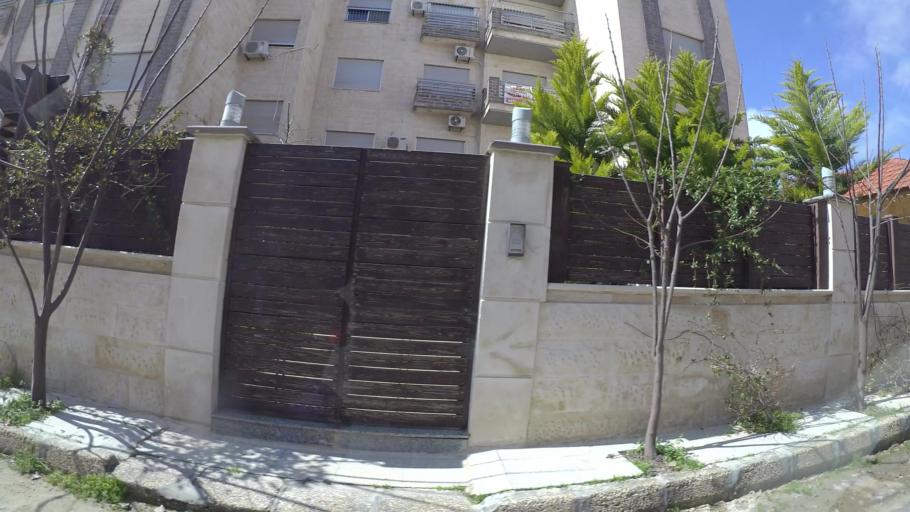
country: JO
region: Amman
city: Wadi as Sir
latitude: 31.9632
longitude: 35.8419
